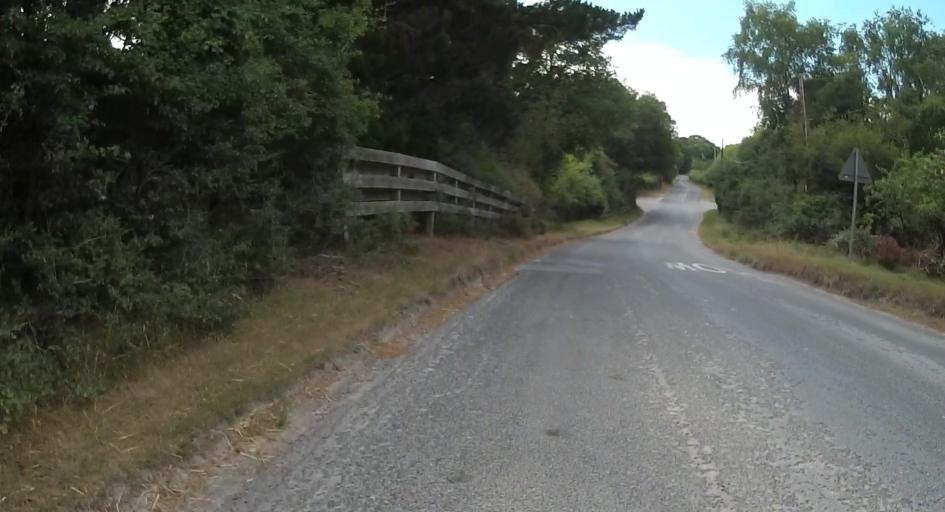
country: GB
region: England
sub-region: Dorset
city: Wareham
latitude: 50.6551
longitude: -2.0986
